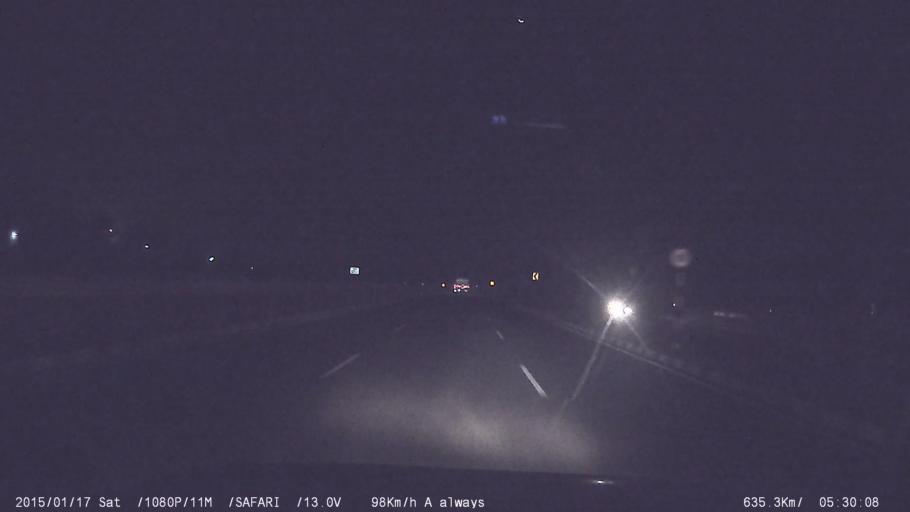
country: IN
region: Tamil Nadu
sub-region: Vellore
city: Arcot
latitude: 12.9123
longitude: 79.2960
